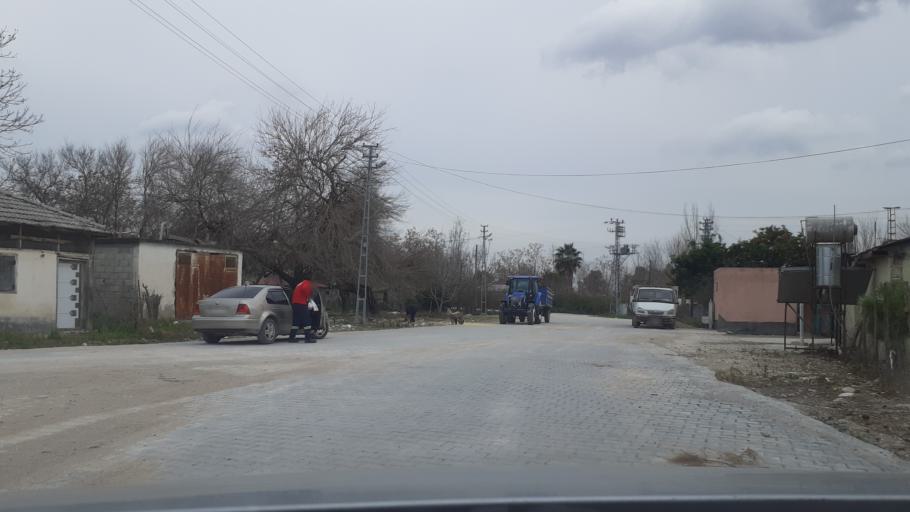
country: TR
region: Osmaniye
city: Sumbas
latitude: 37.3735
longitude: 35.9727
